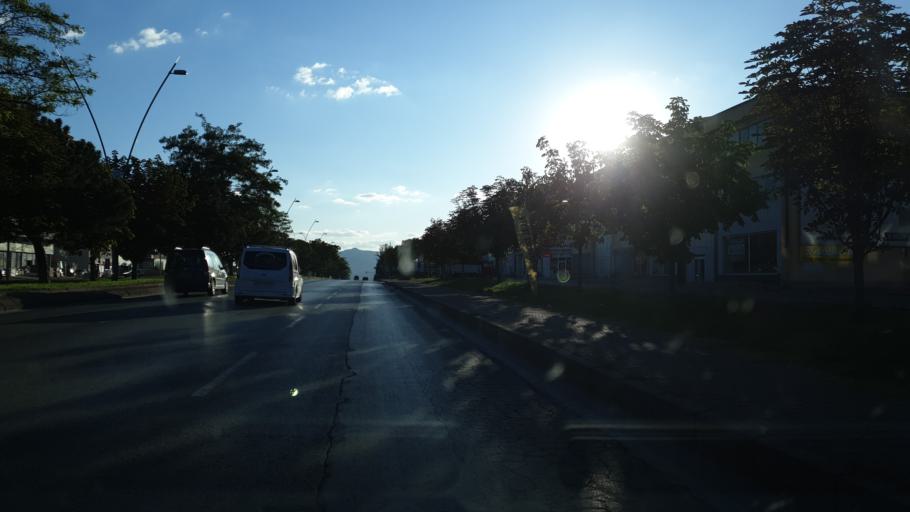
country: TR
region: Kayseri
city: Kocasinan
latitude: 38.7461
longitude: 35.5324
